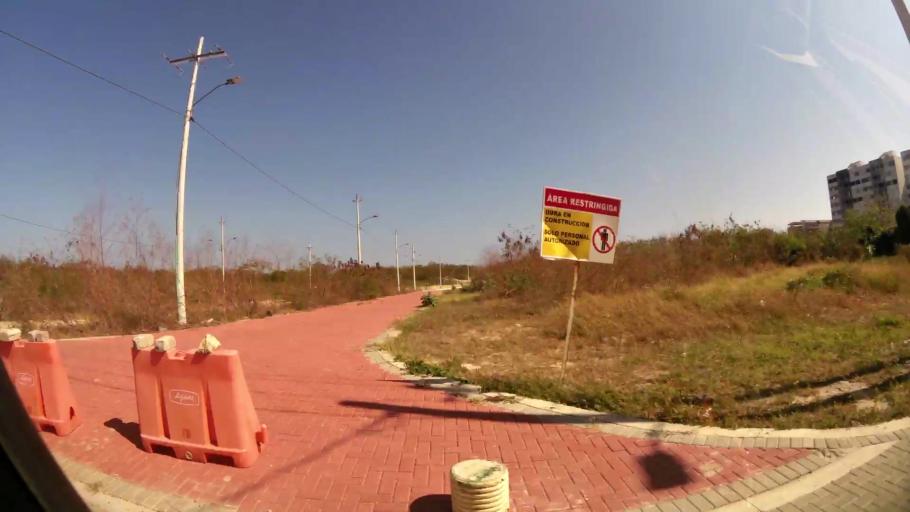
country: CO
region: Atlantico
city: Barranquilla
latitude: 11.0229
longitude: -74.8180
